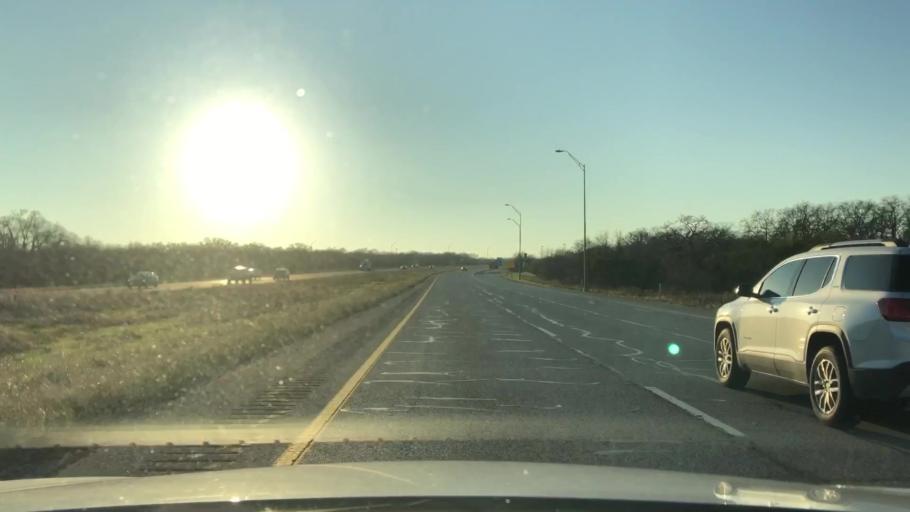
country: US
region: Texas
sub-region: Caldwell County
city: Luling
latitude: 29.6164
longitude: -97.8011
